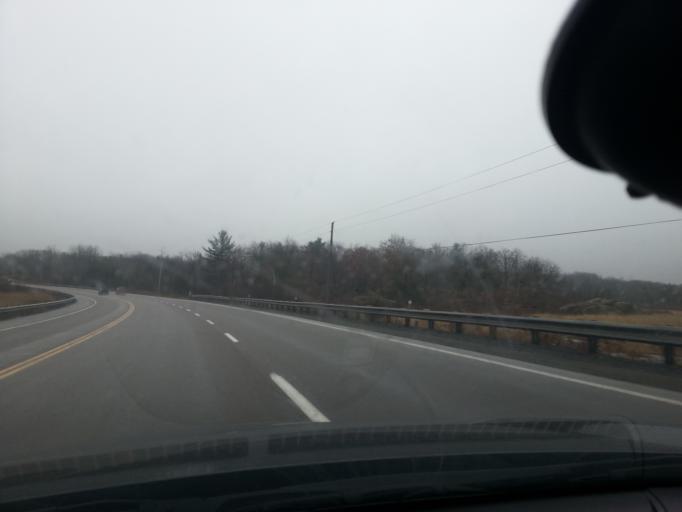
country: CA
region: Ontario
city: Quinte West
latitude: 44.4939
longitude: -77.5790
